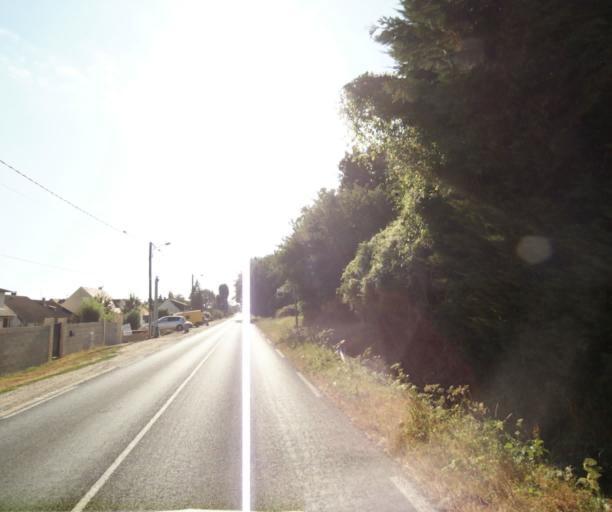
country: FR
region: Ile-de-France
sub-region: Departement de l'Essonne
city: Itteville
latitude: 48.5128
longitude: 2.3301
